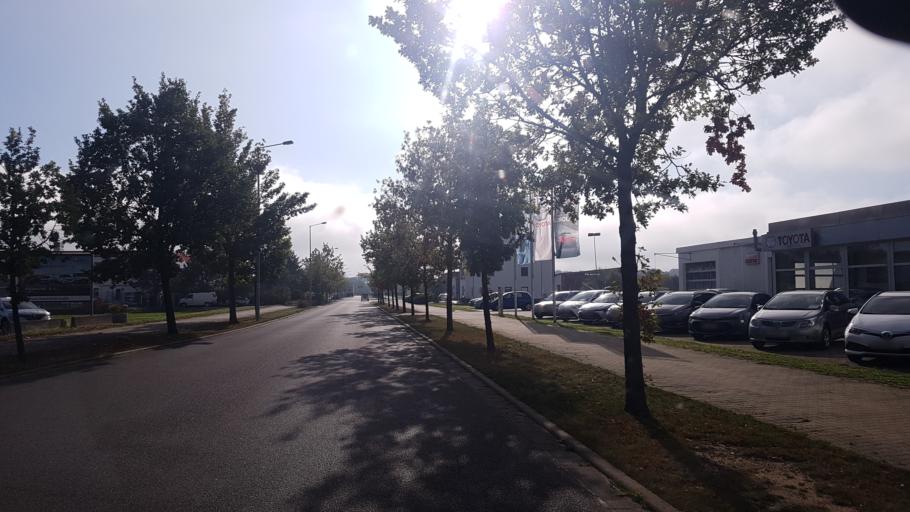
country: DE
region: Brandenburg
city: Elsterwerda
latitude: 51.4637
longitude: 13.5382
